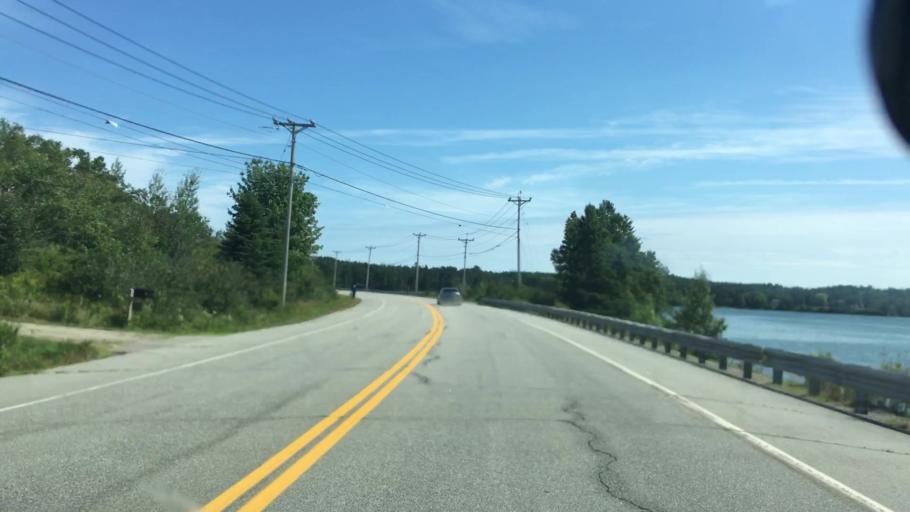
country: US
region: Maine
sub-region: Washington County
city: Eastport
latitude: 44.9401
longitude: -67.0360
